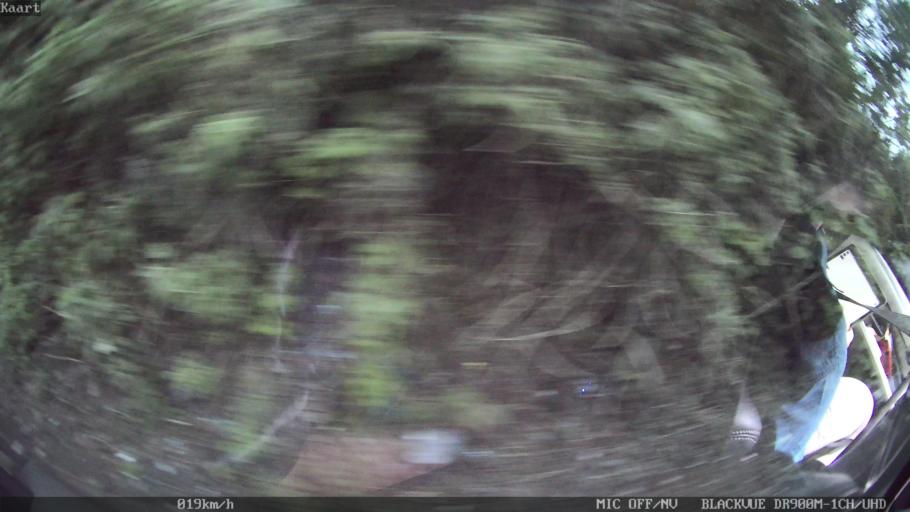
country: ID
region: Bali
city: Banjar Kedisan
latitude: -8.2595
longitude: 115.3383
